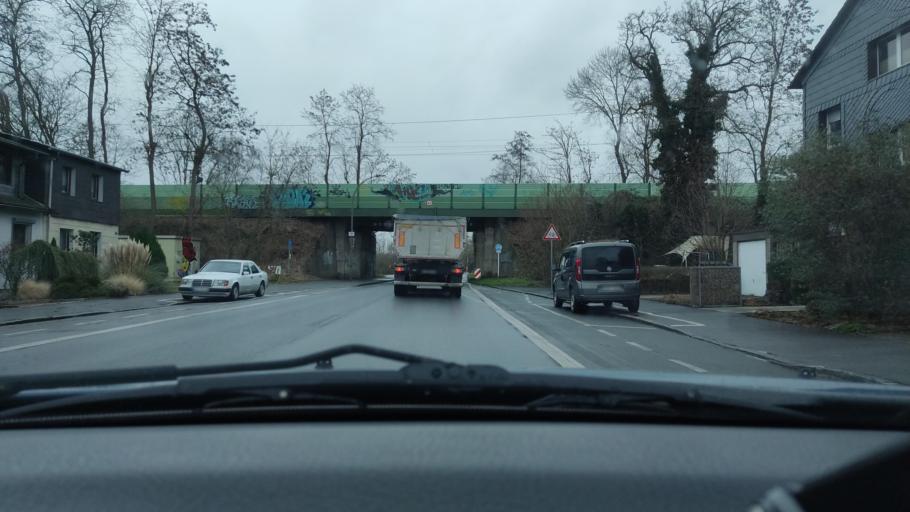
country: DE
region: North Rhine-Westphalia
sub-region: Regierungsbezirk Arnsberg
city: Dortmund
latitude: 51.5513
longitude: 7.4266
